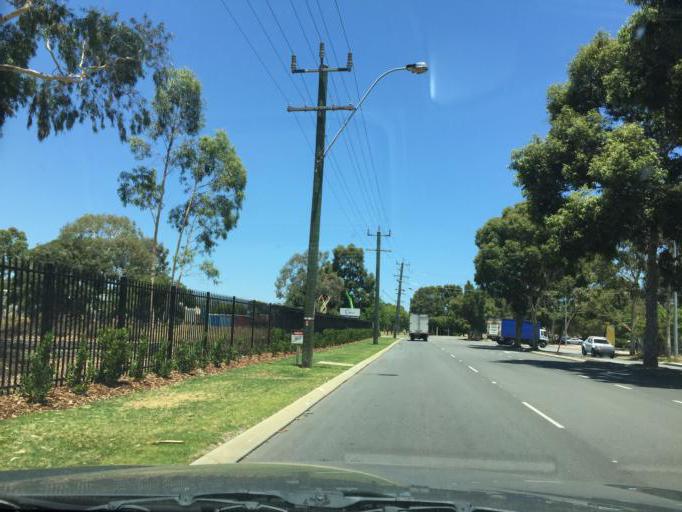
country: AU
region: Western Australia
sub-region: Canning
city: Canning Vale
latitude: -32.0617
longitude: 115.9291
